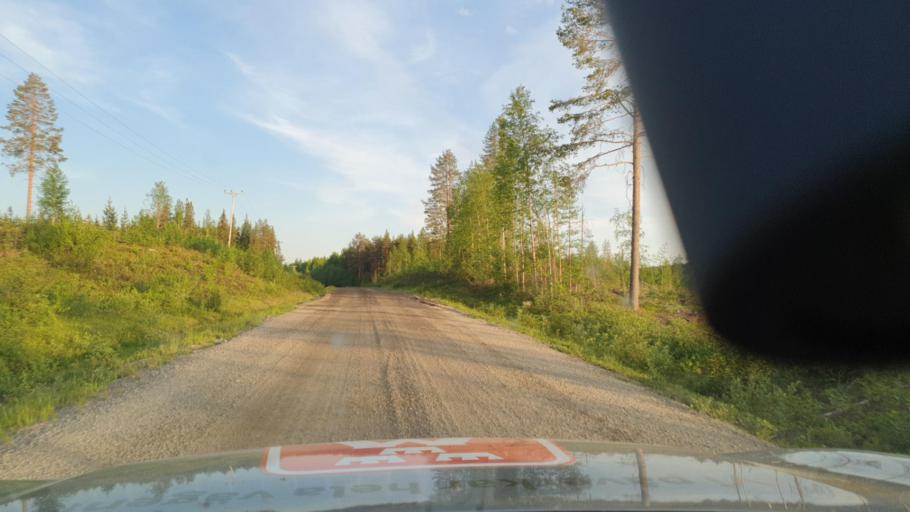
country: SE
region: Norrbotten
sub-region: Bodens Kommun
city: Boden
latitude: 66.1861
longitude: 21.5023
